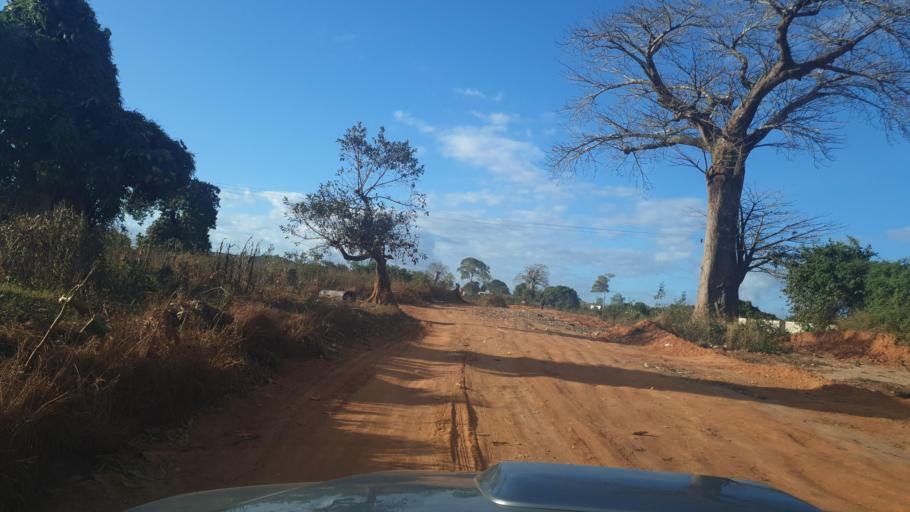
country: MZ
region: Nampula
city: Nampula
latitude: -15.1538
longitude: 39.2657
